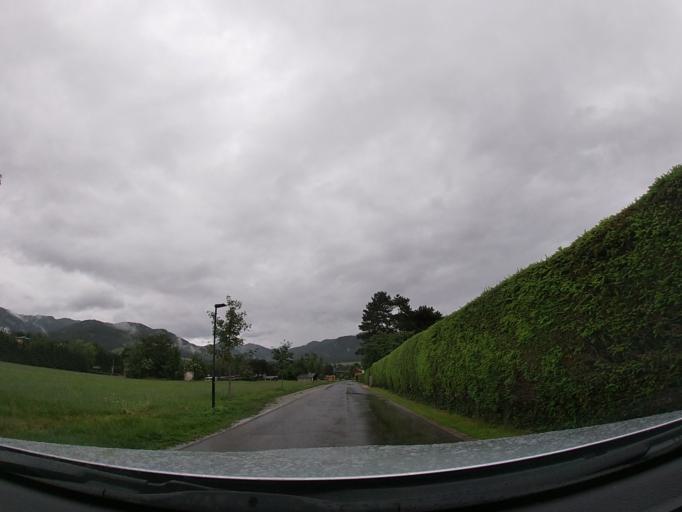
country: AT
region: Styria
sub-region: Politischer Bezirk Leoben
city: Trofaiach
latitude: 47.4204
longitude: 14.9977
